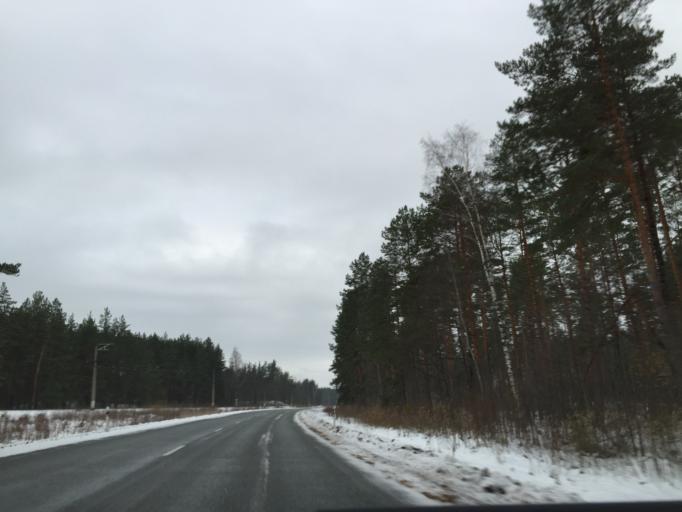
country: LV
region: Saulkrastu
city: Saulkrasti
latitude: 57.2083
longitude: 24.3802
